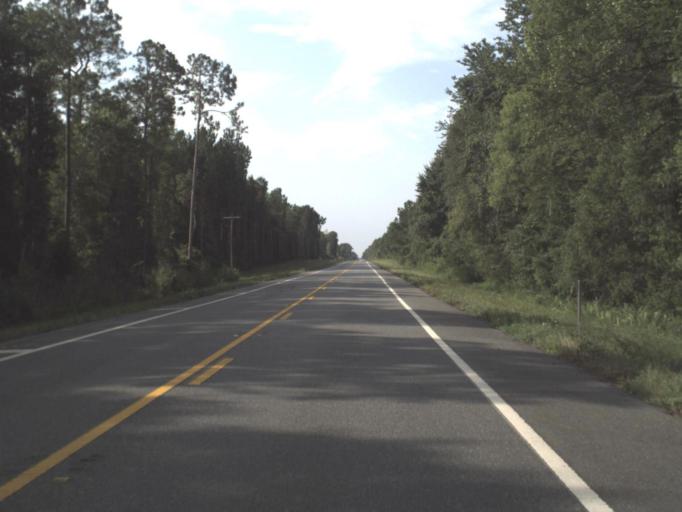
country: US
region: Florida
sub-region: Taylor County
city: Perry
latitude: 30.2683
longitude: -83.6273
